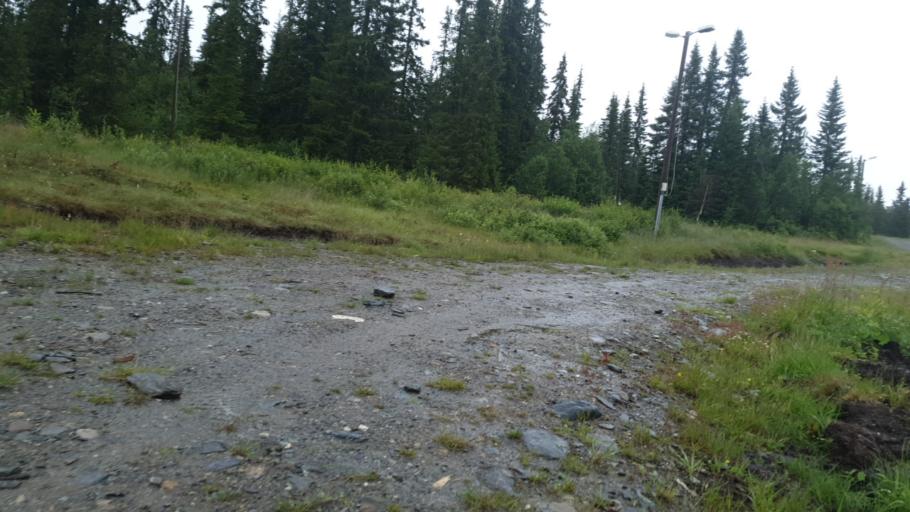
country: NO
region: Oppland
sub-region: Vestre Slidre
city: Slidre
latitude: 61.2335
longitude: 8.9168
